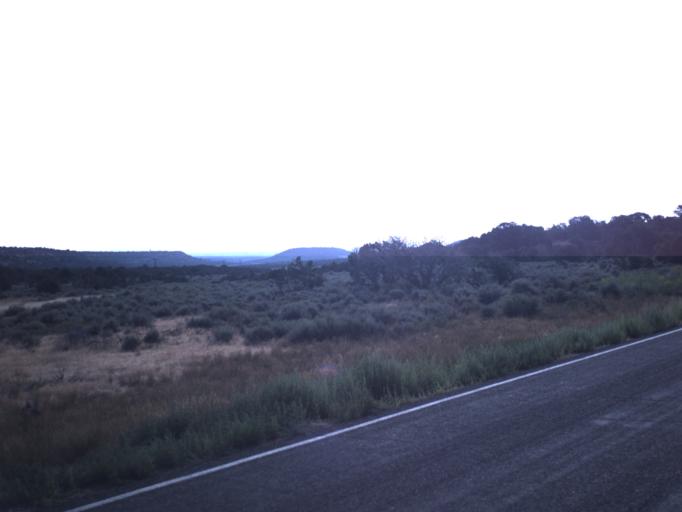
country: US
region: Utah
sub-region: Duchesne County
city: Duchesne
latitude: 40.3185
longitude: -110.3937
